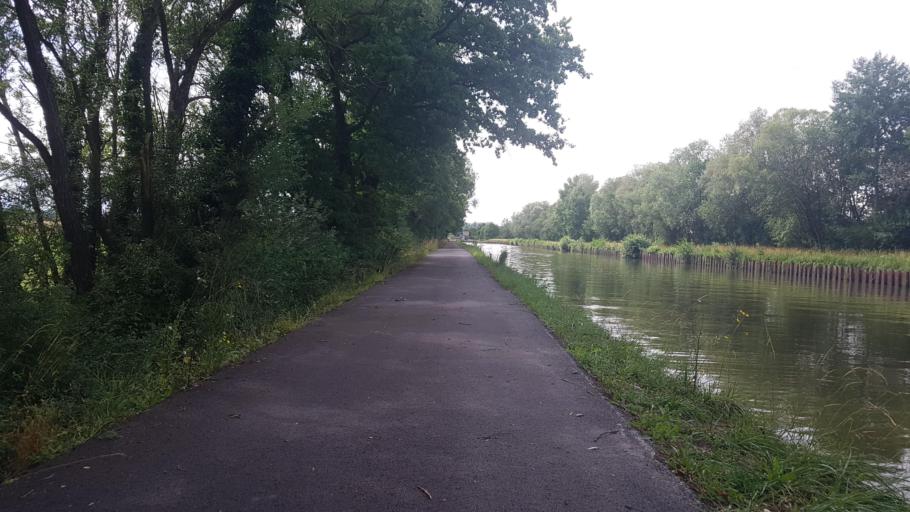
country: FR
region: Lorraine
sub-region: Departement de la Moselle
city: Dieuze
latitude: 48.6858
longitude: 6.7753
